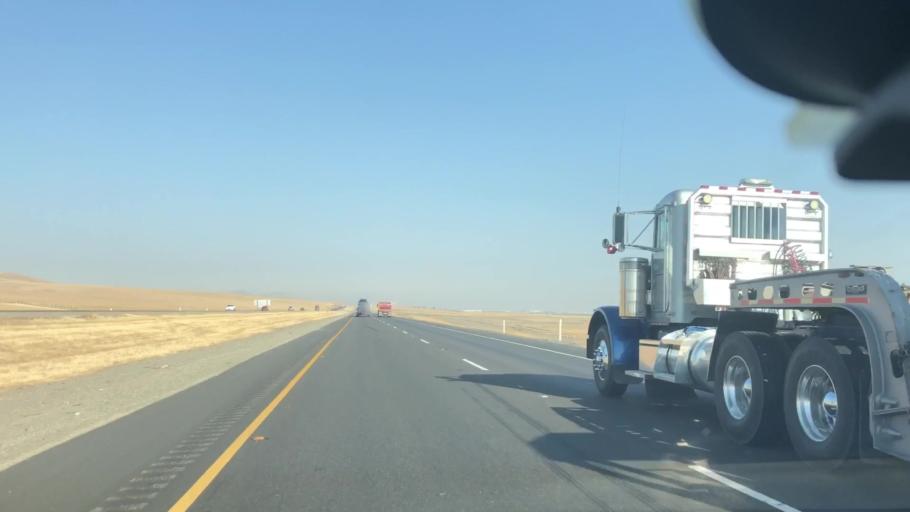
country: US
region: California
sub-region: San Joaquin County
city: Tracy
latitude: 37.6804
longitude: -121.4705
